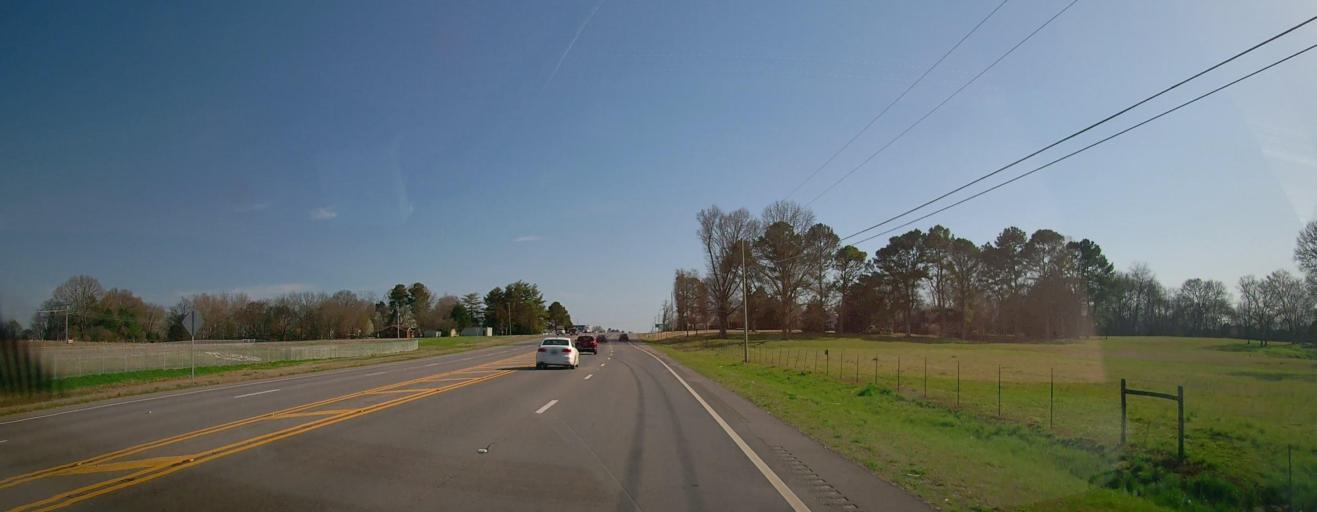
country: US
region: Alabama
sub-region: Colbert County
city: Muscle Shoals
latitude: 34.7122
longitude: -87.6350
